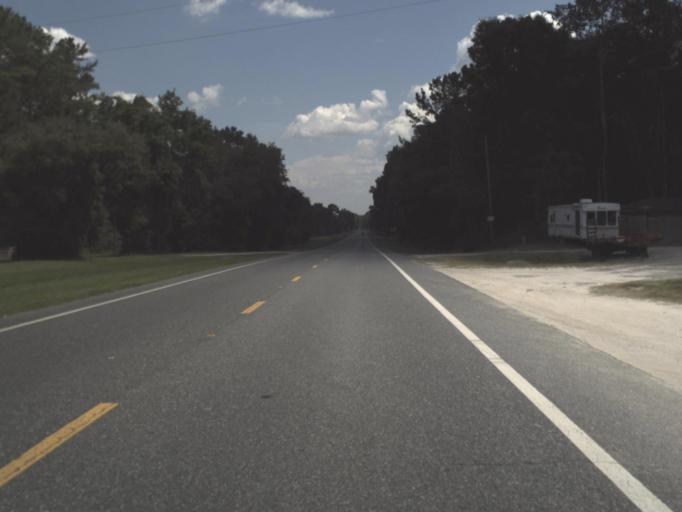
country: US
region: Florida
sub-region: Alachua County
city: High Springs
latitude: 29.8620
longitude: -82.6087
